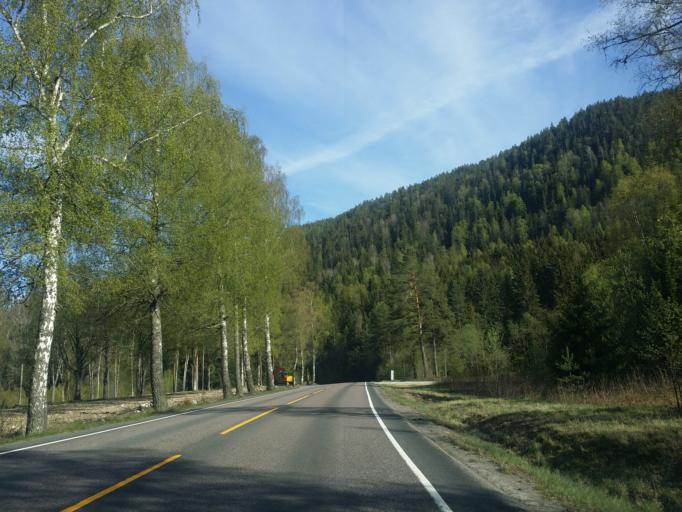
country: NO
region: Telemark
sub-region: Hjartdal
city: Sauland
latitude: 59.6101
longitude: 8.9701
